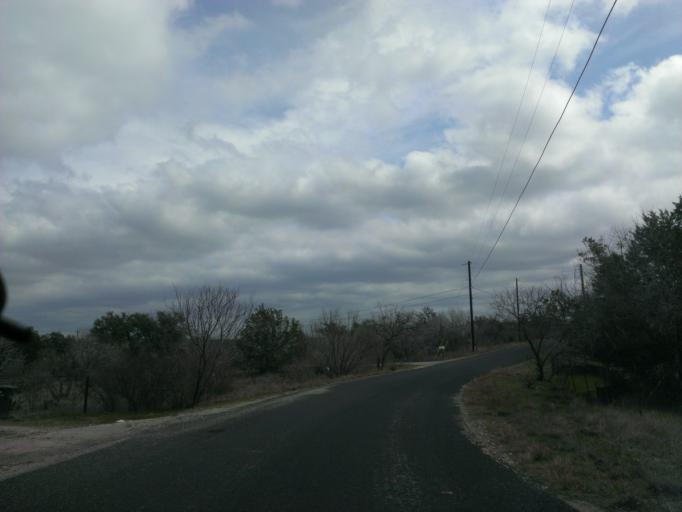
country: US
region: Texas
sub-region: Travis County
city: Briarcliff
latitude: 30.3934
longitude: -98.1030
